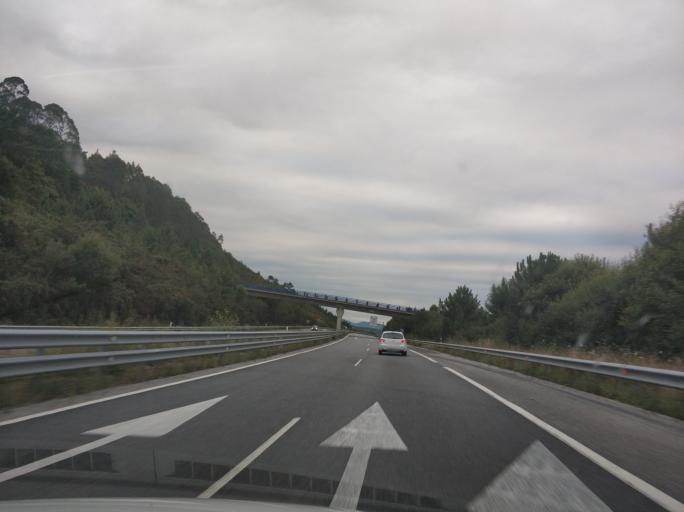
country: ES
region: Asturias
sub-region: Province of Asturias
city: Tineo
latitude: 43.5454
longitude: -6.4380
